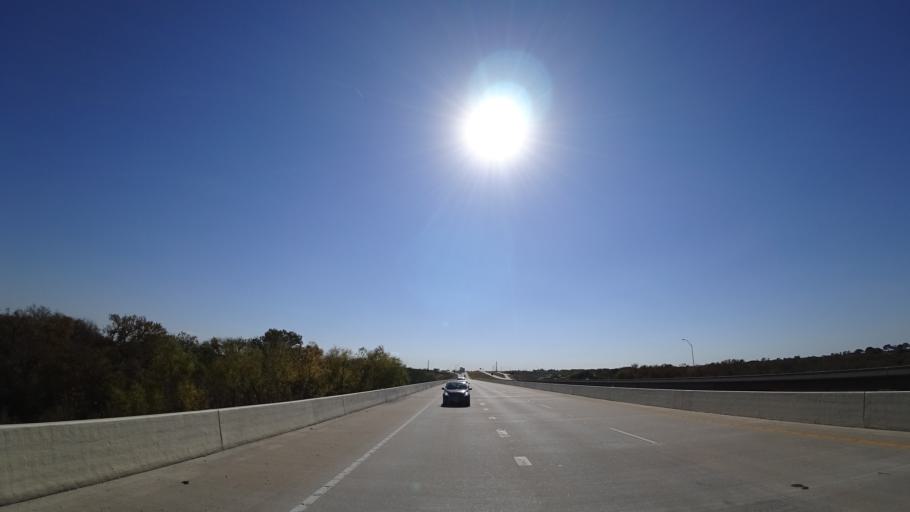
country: US
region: Texas
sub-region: Williamson County
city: Hutto
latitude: 30.5263
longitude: -97.5756
